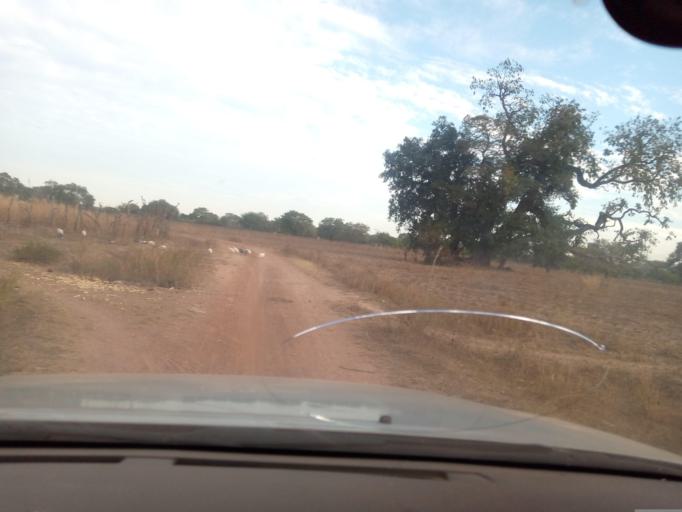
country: ML
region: Sikasso
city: Kadiolo
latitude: 10.5847
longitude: -5.8481
